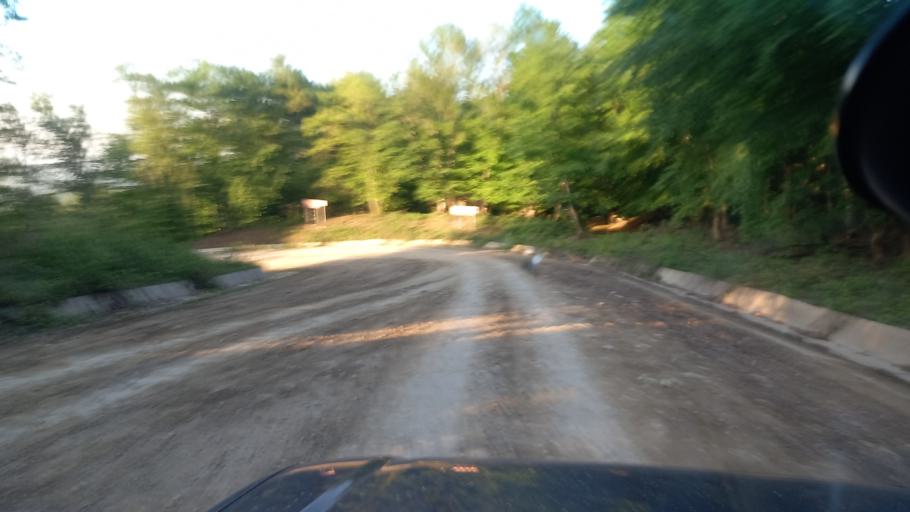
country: RU
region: Dagestan
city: Khuchni
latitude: 42.0037
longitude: 47.9755
